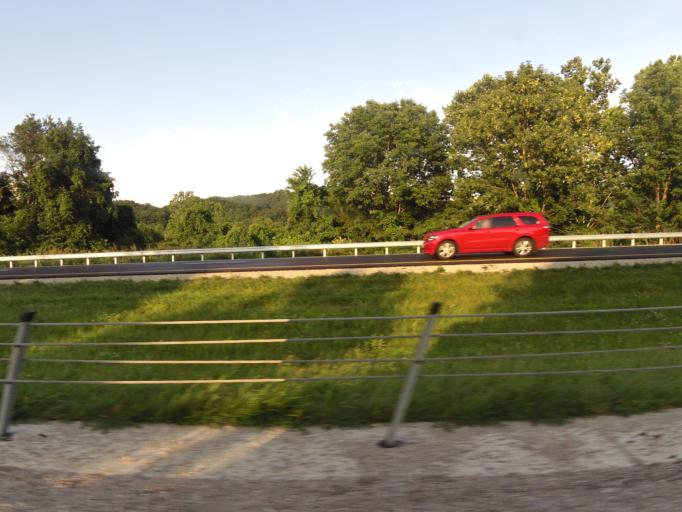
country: US
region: Kentucky
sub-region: Rockcastle County
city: Brodhead
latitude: 37.4651
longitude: -84.3355
